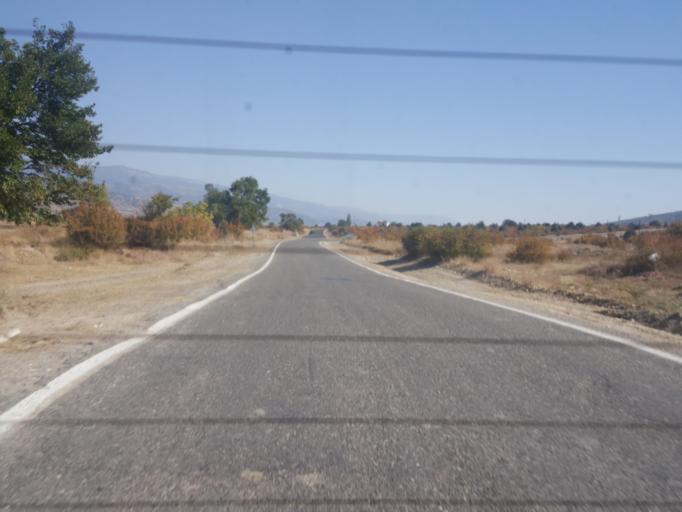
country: TR
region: Kastamonu
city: Tosya
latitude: 41.0006
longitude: 34.1470
